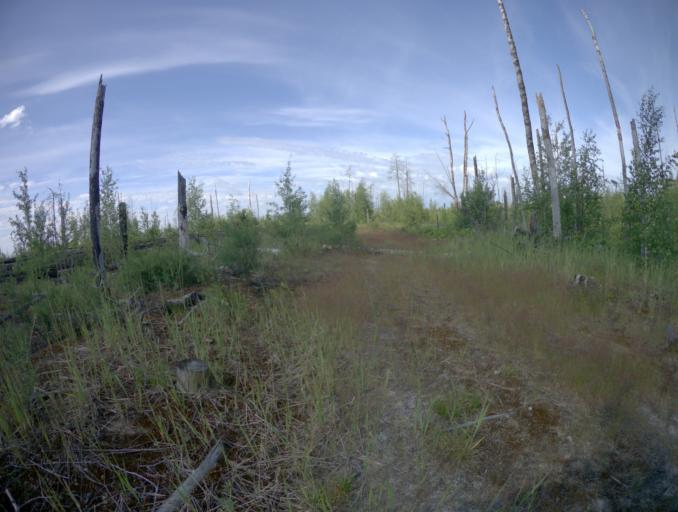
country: RU
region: Ivanovo
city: Talitsy
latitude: 56.5117
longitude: 42.3735
